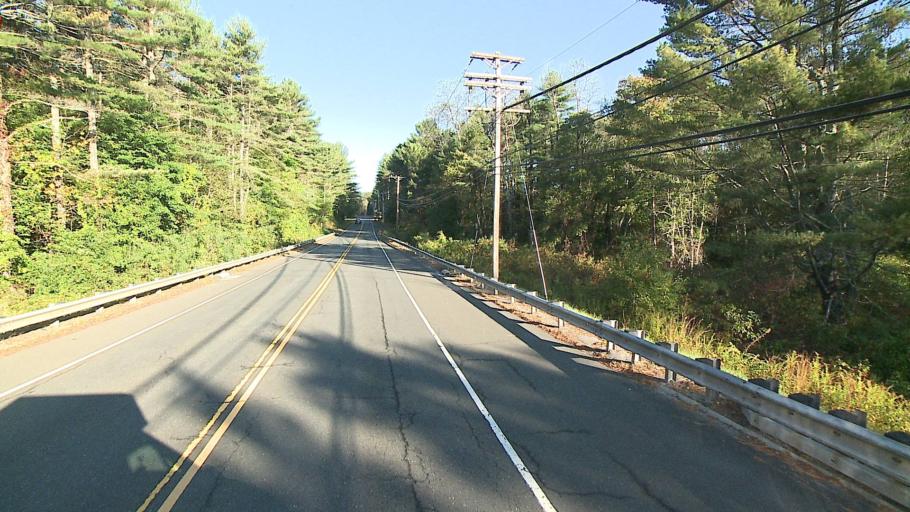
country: US
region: Connecticut
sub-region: Litchfield County
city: New Hartford Center
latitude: 41.8261
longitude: -72.9748
